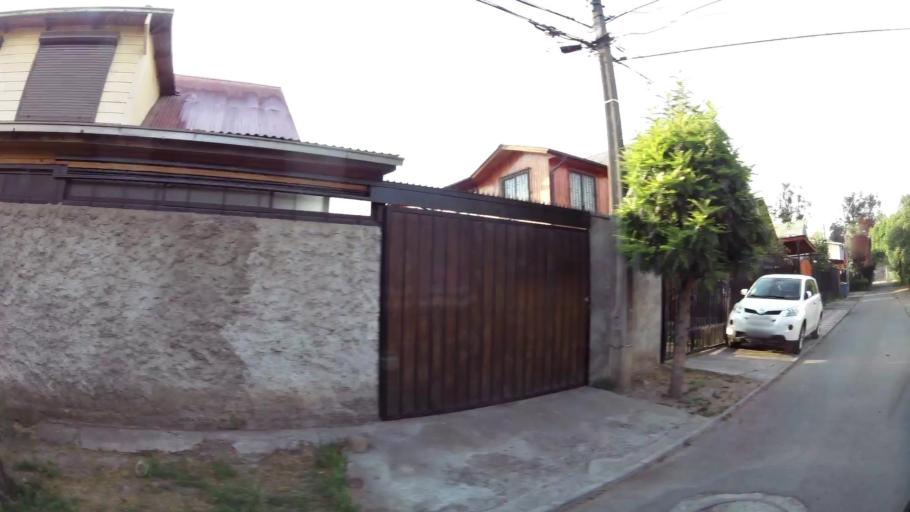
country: CL
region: Santiago Metropolitan
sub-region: Provincia de Santiago
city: Villa Presidente Frei, Nunoa, Santiago, Chile
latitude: -33.5209
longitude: -70.5881
